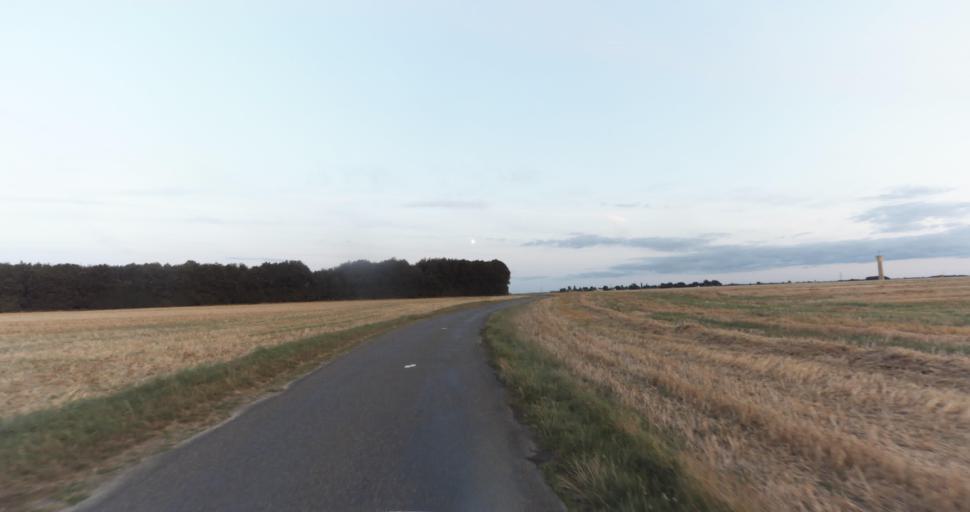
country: FR
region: Haute-Normandie
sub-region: Departement de l'Eure
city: La Madeleine-de-Nonancourt
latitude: 48.8799
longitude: 1.2411
